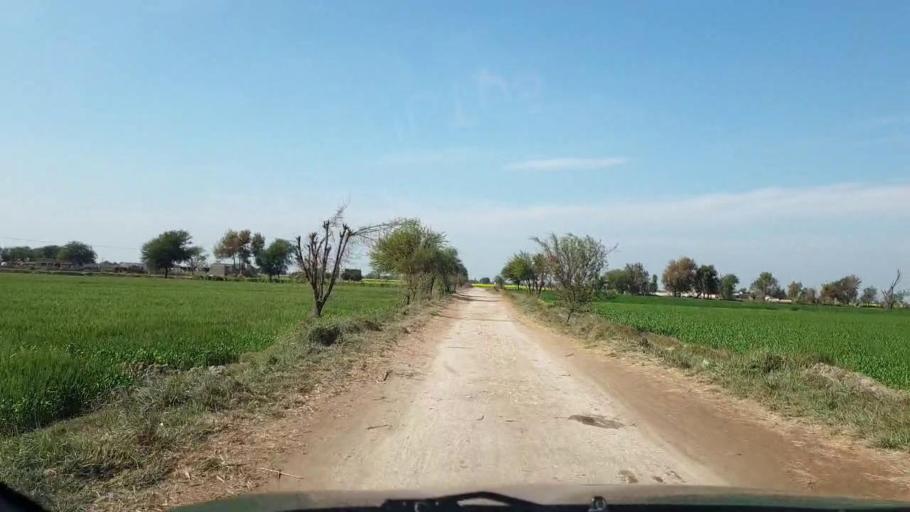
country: PK
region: Sindh
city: Sinjhoro
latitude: 25.9771
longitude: 68.7928
